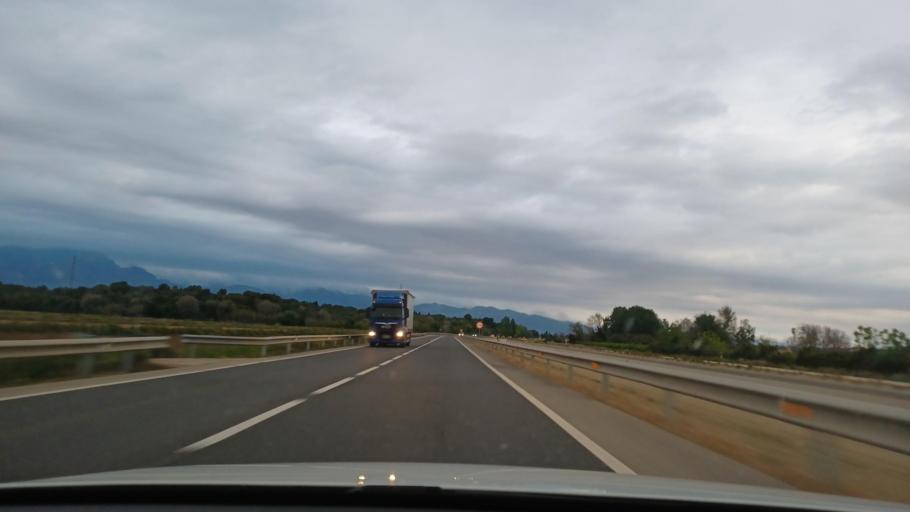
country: ES
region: Catalonia
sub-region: Provincia de Tarragona
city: Masdenverge
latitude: 40.7575
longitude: 0.5373
